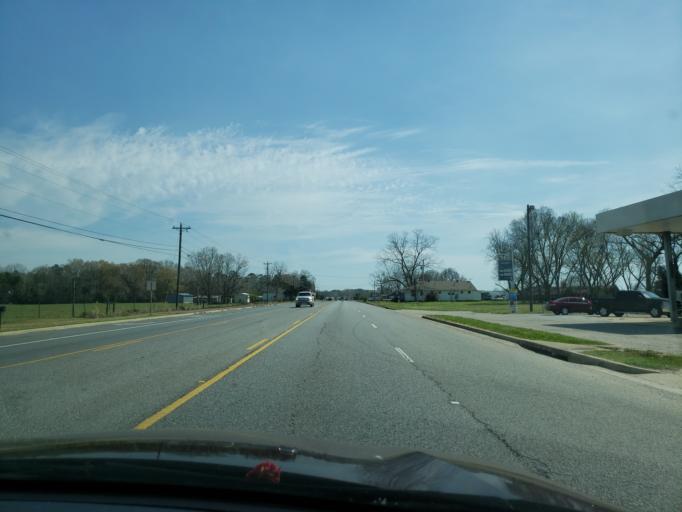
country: US
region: Alabama
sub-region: Elmore County
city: Wetumpka
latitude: 32.5383
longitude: -86.2629
